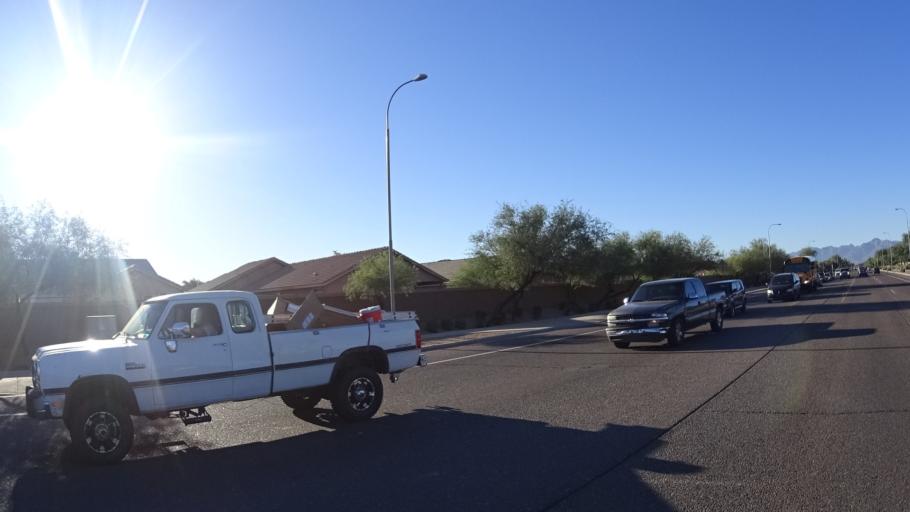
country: US
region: Arizona
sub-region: Maricopa County
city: Tolleson
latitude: 33.4334
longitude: -112.2384
